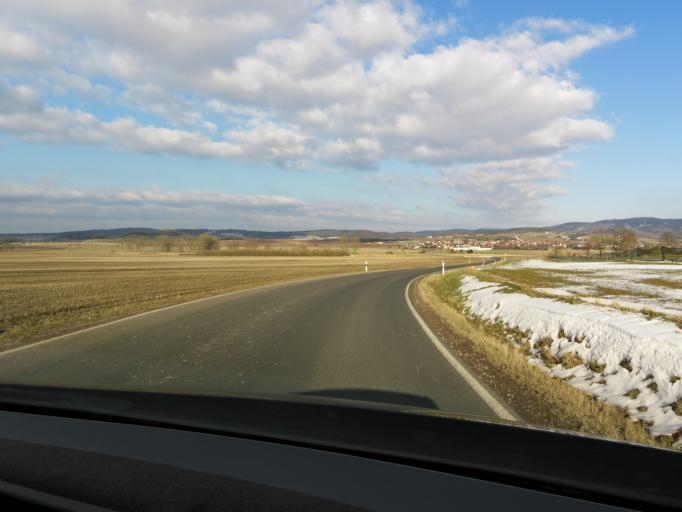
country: DE
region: Thuringia
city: Bad Salzungen
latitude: 50.8524
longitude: 10.2296
